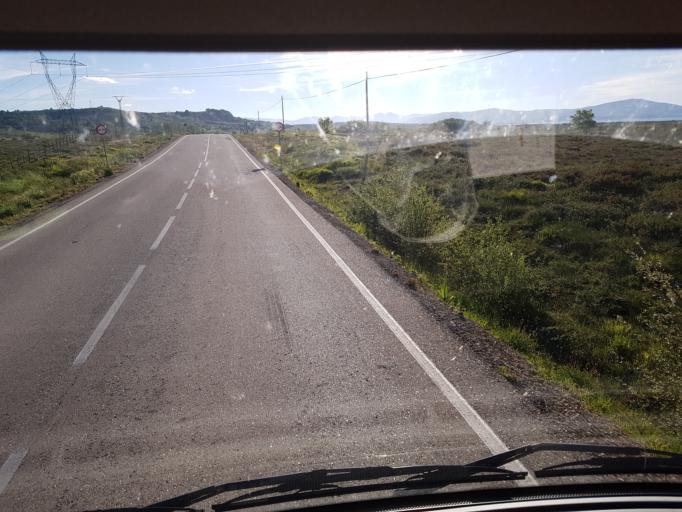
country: ES
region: Castille and Leon
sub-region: Provincia de Burgos
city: Arija
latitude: 42.9771
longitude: -3.8686
